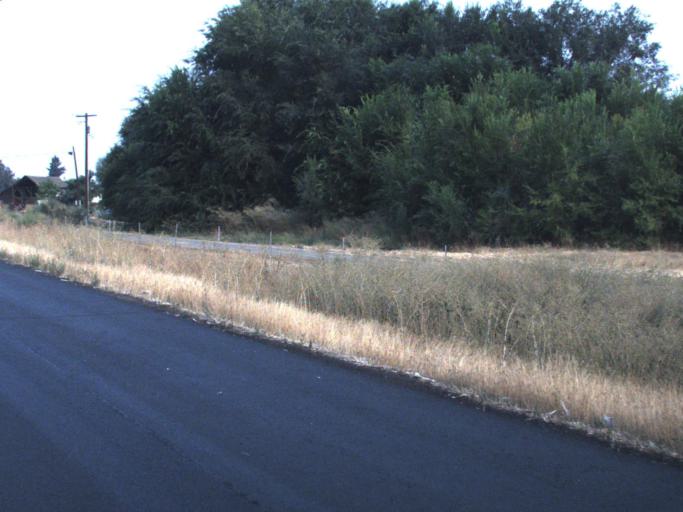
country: US
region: Washington
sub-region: Yakima County
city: Wapato
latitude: 46.4091
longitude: -120.3853
